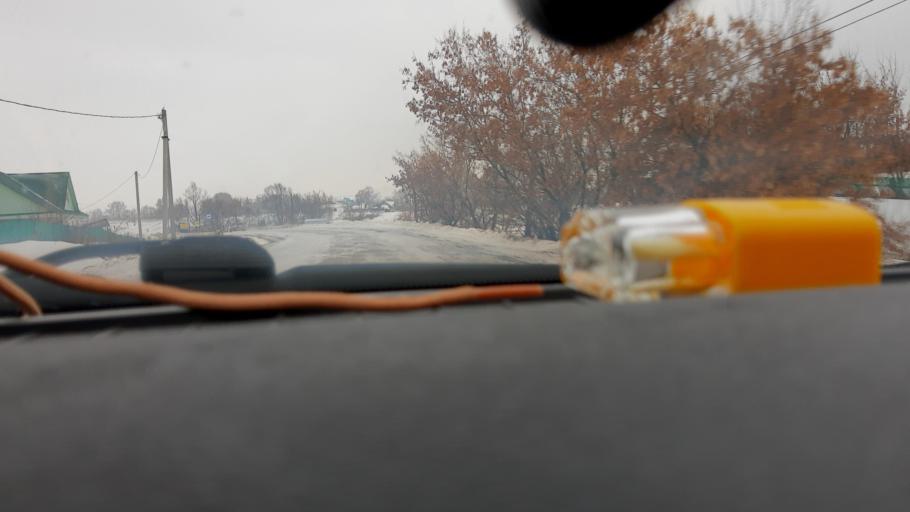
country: RU
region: Bashkortostan
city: Ulukulevo
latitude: 54.5112
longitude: 56.4110
